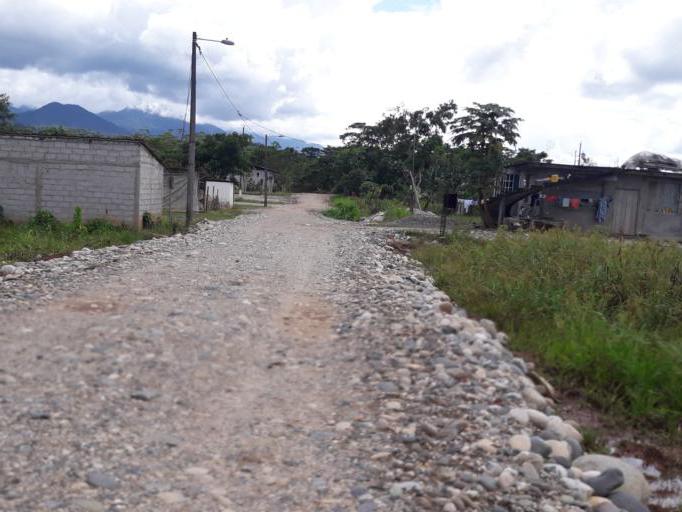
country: EC
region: Napo
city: Tena
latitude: -0.9551
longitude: -77.8170
